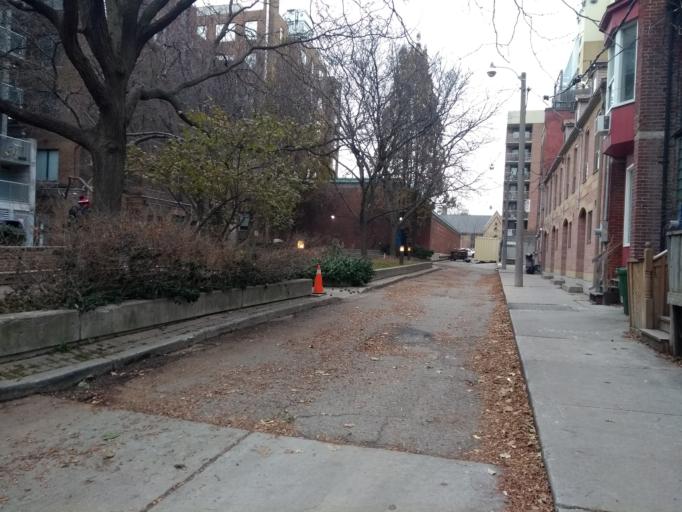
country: CA
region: Ontario
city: Toronto
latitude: 43.6506
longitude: -79.3904
